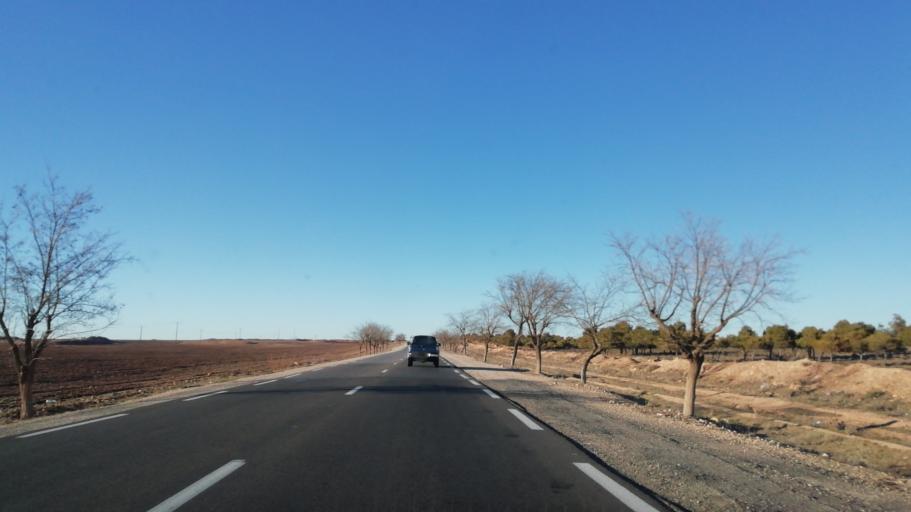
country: DZ
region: Tlemcen
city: Sebdou
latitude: 34.5348
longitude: -1.2977
